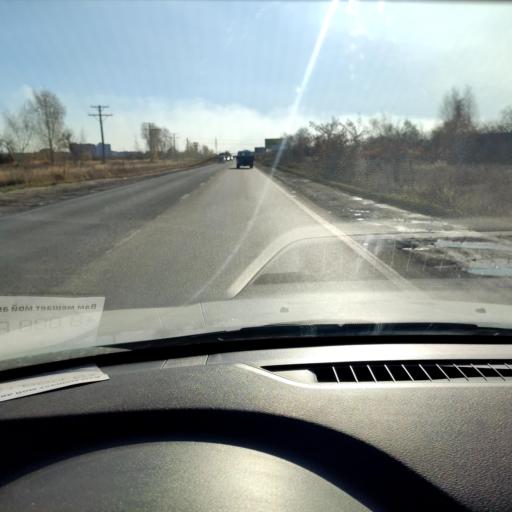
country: RU
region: Samara
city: Tol'yatti
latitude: 53.5500
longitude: 49.3733
